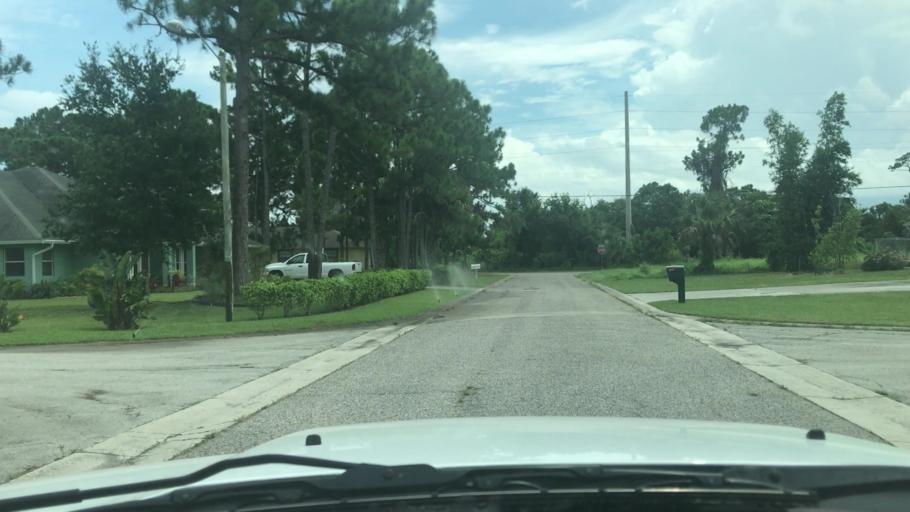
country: US
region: Florida
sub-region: Indian River County
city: Florida Ridge
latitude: 27.5589
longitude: -80.3857
